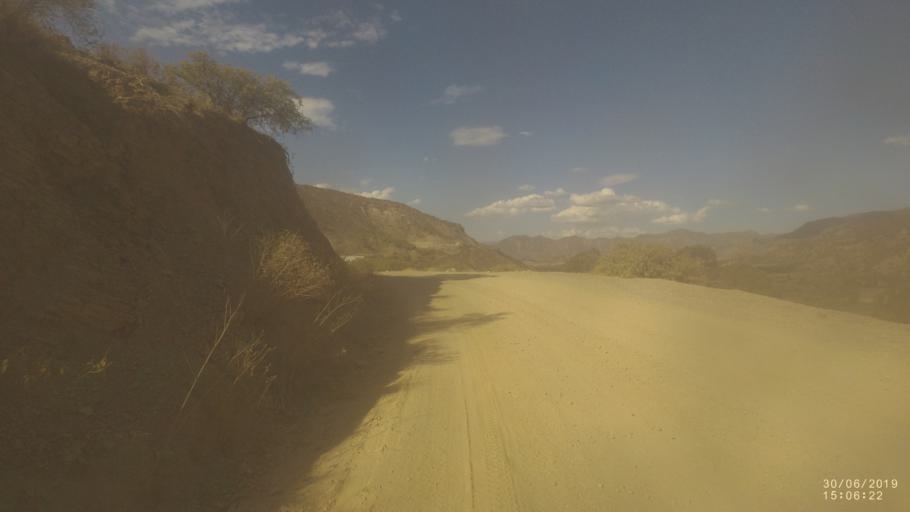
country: BO
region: Cochabamba
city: Irpa Irpa
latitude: -17.7322
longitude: -66.3115
